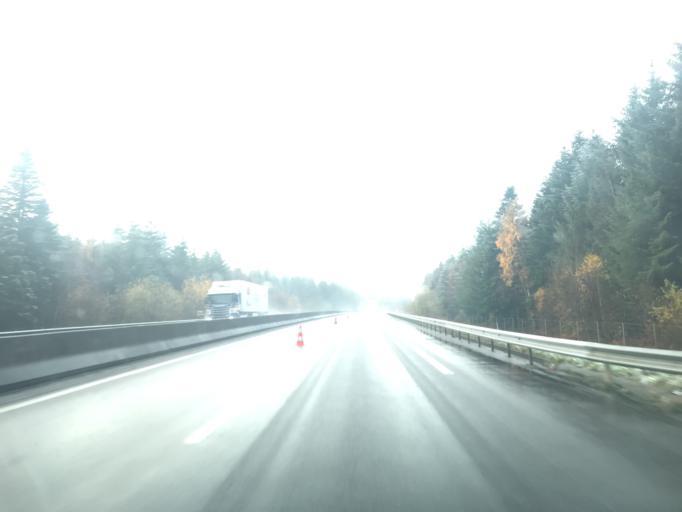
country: FR
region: Lower Normandy
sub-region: Departement de l'Orne
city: Gace
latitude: 48.8005
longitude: 0.3406
